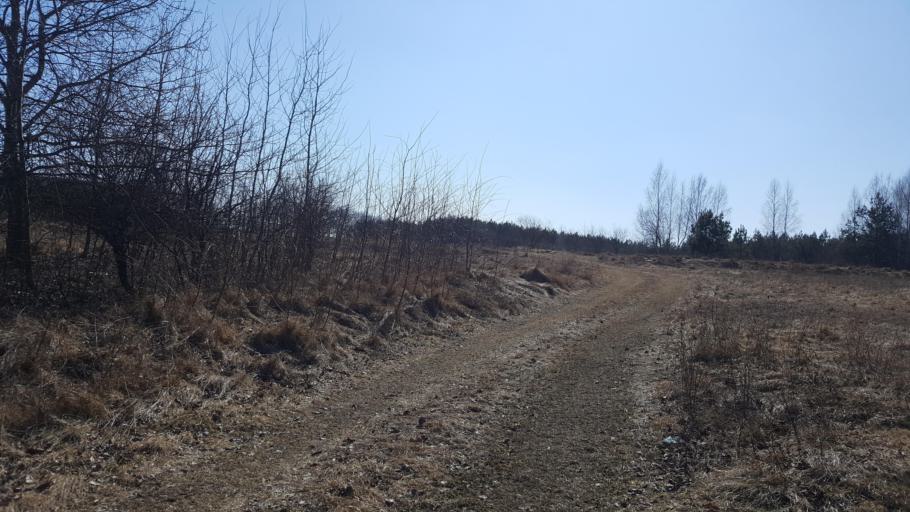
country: BY
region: Brest
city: Kamyanyets
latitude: 52.3739
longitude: 23.7757
